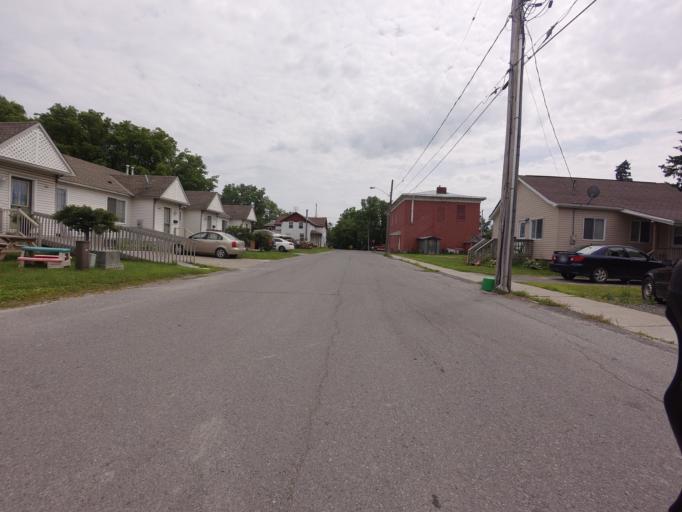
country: CA
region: Ontario
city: Prescott
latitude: 45.0187
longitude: -75.6464
